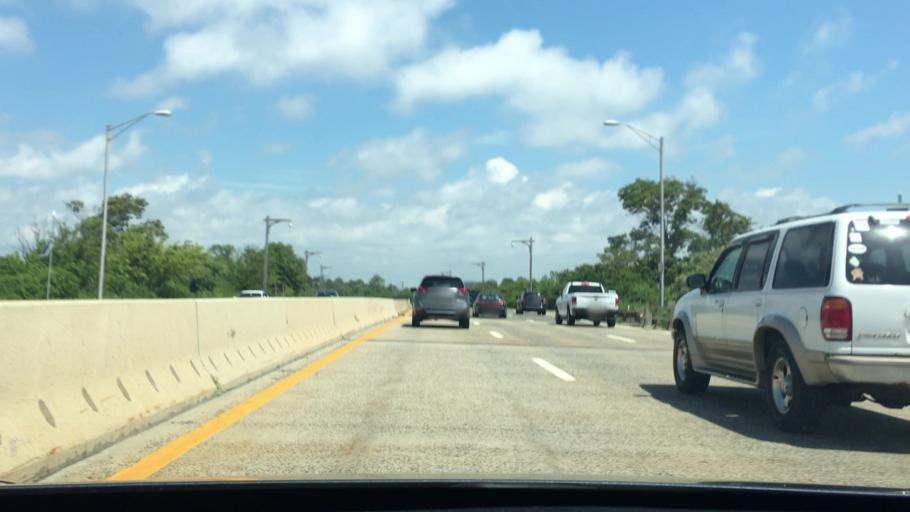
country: US
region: New York
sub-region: Nassau County
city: Freeport
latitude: 40.6299
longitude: -73.5625
